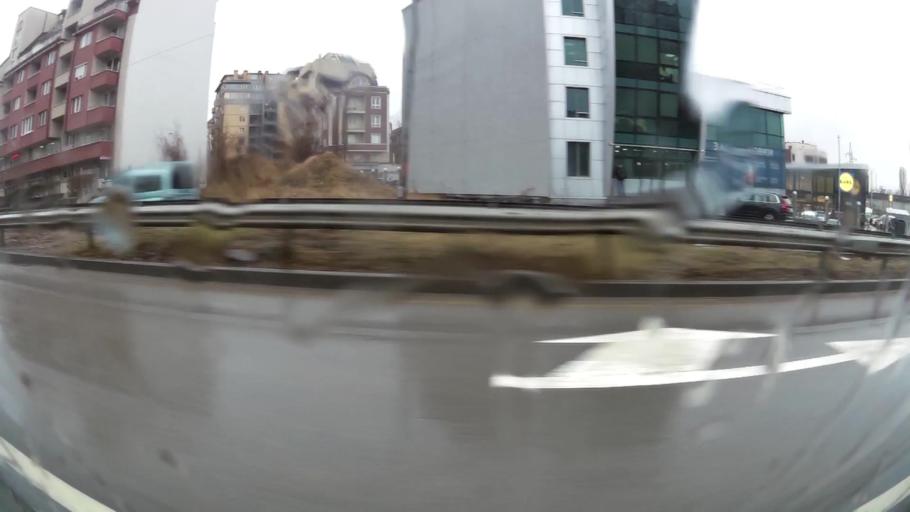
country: BG
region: Sofia-Capital
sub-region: Stolichna Obshtina
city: Sofia
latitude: 42.6496
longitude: 23.3693
